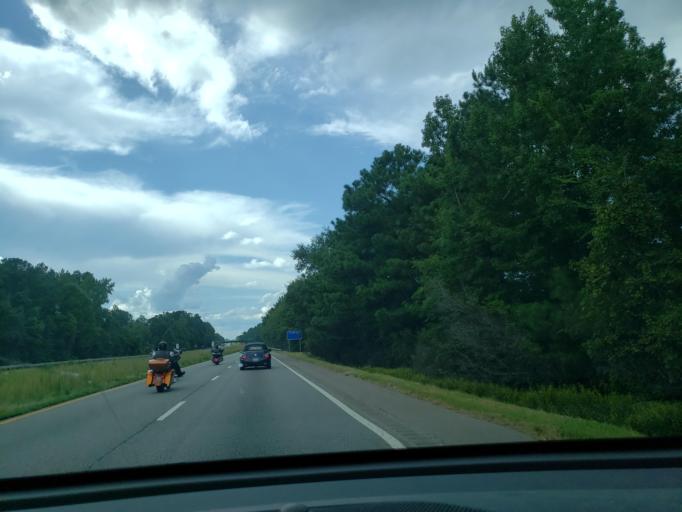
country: US
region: Virginia
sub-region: City of Franklin
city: Franklin
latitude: 36.6428
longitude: -76.9021
